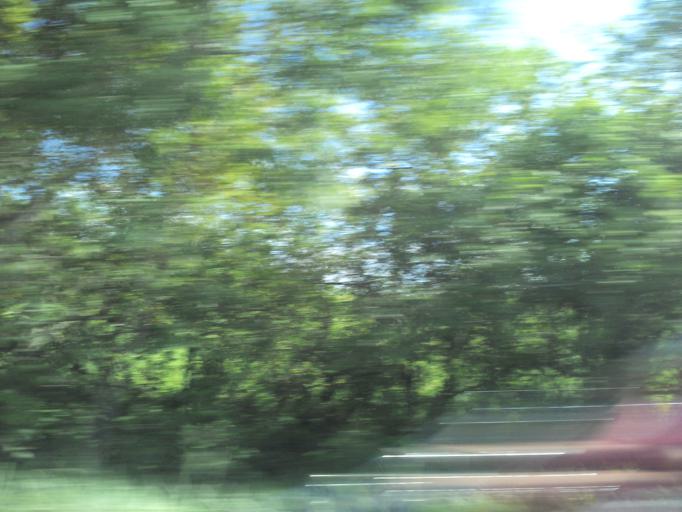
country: MX
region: Chiapas
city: Palenque
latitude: 17.5524
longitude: -91.9959
